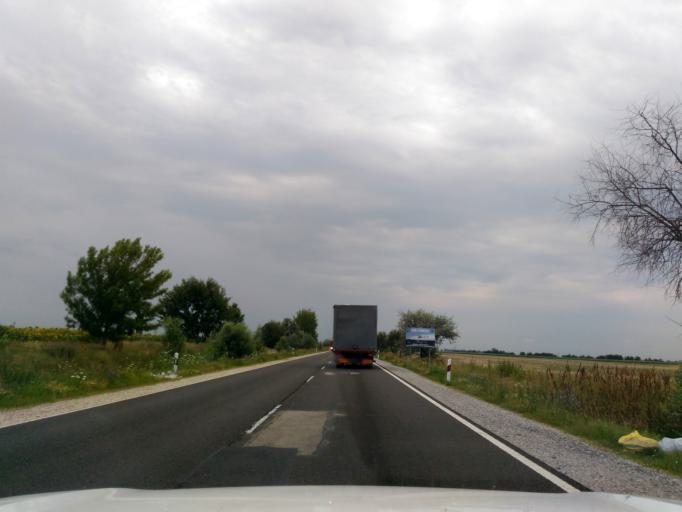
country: HU
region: Jasz-Nagykun-Szolnok
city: Toszeg
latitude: 47.1685
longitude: 20.1040
